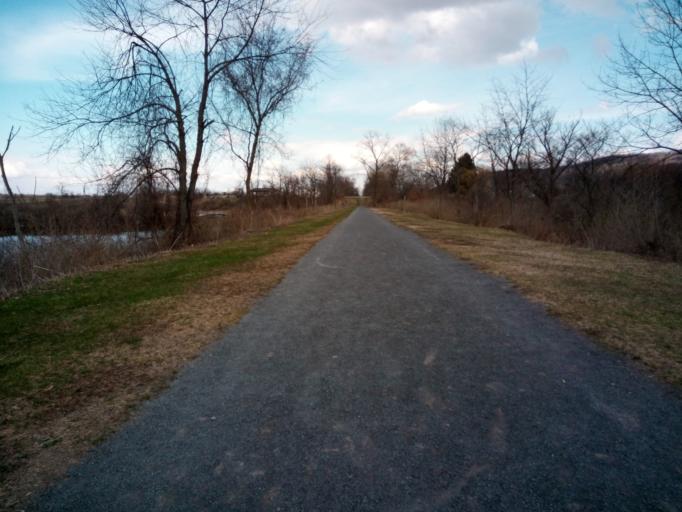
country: US
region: New York
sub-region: Chemung County
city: Big Flats
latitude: 42.1442
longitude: -76.9134
